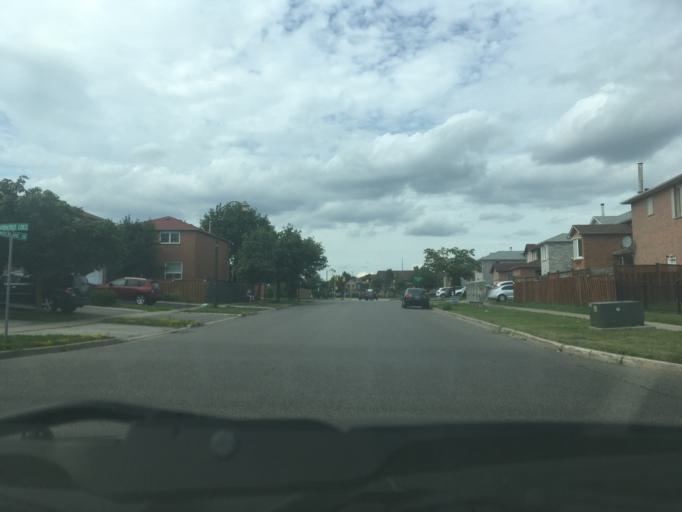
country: CA
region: Ontario
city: Brampton
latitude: 43.6517
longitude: -79.7322
